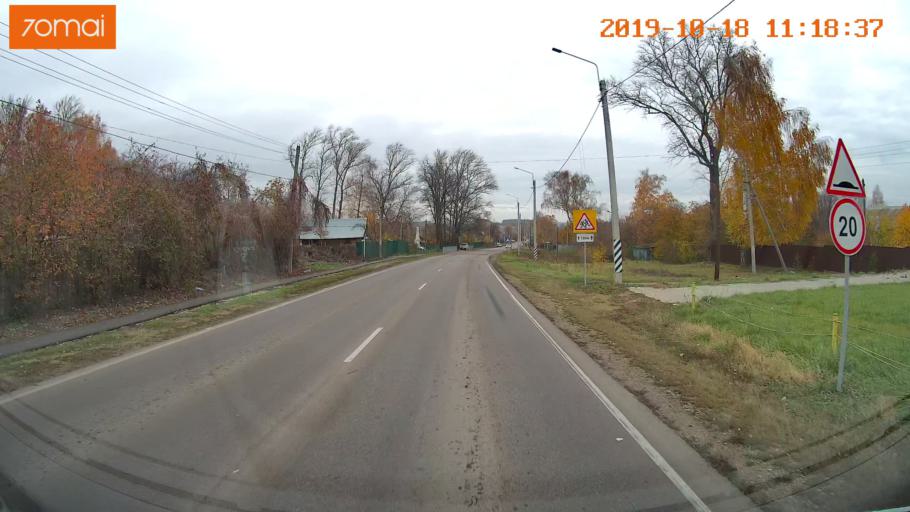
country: RU
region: Tula
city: Kimovsk
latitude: 54.0405
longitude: 38.5507
